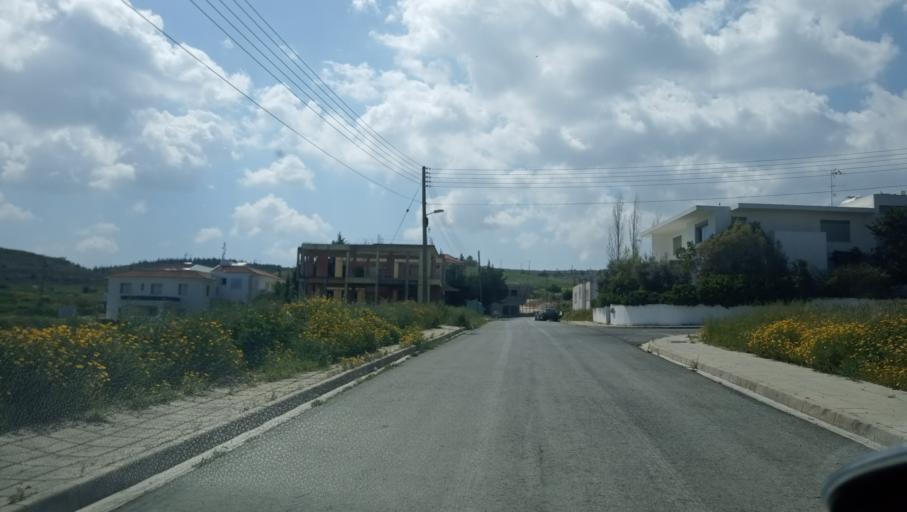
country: CY
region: Lefkosia
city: Alampra
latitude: 35.0112
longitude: 33.4019
